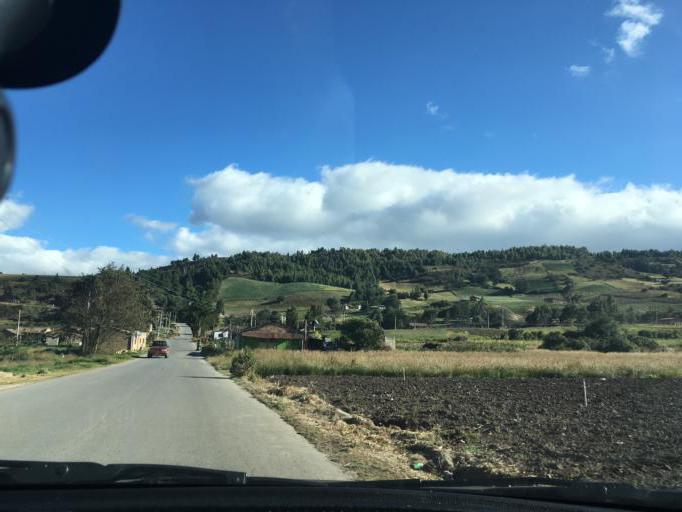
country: CO
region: Boyaca
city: Pesca
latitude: 5.5131
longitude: -72.9753
